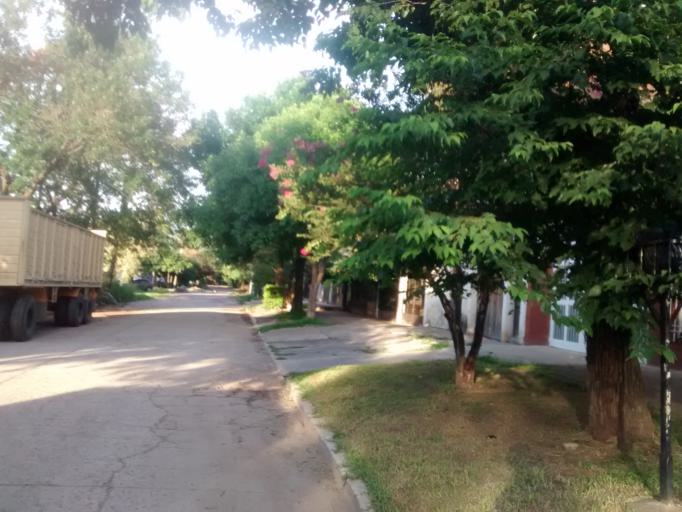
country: AR
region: Chaco
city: Resistencia
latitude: -27.4383
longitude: -58.9989
